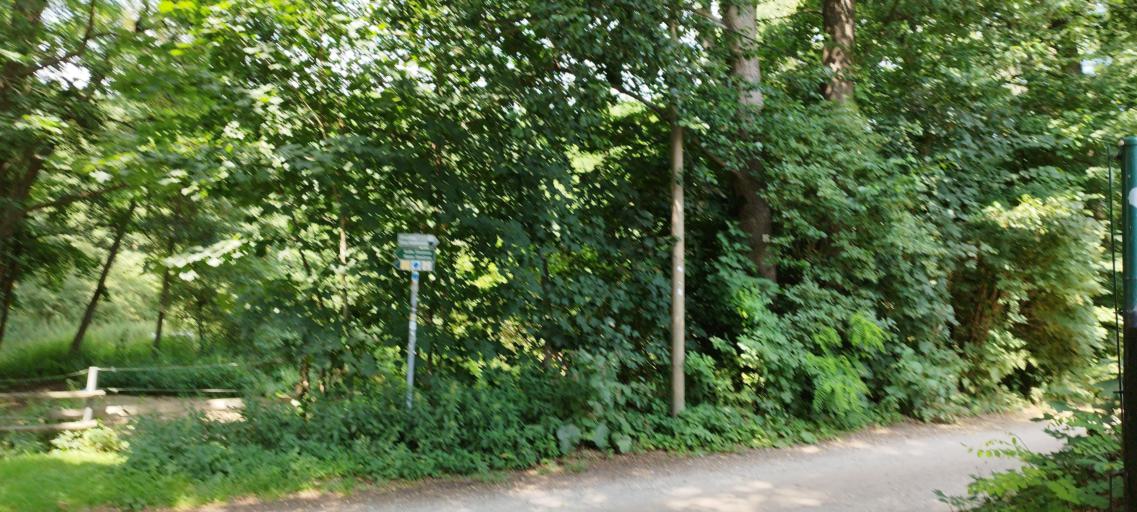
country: DE
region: Brandenburg
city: Rehfelde
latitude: 52.5145
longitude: 13.8525
